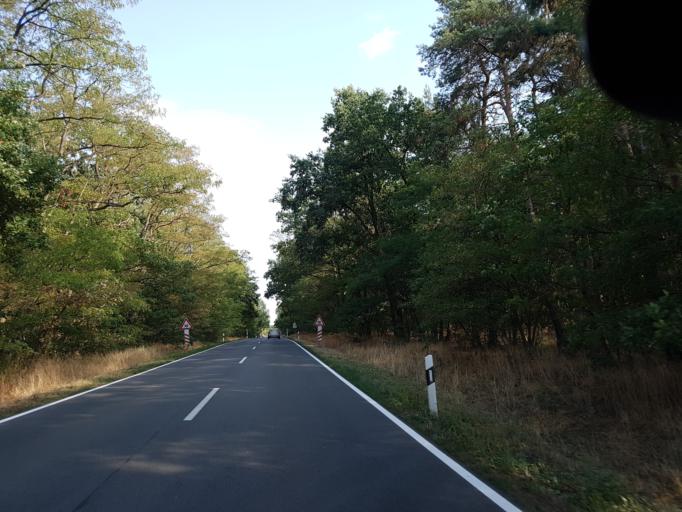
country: DE
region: Saxony-Anhalt
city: Pretzsch
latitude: 51.7332
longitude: 12.7696
